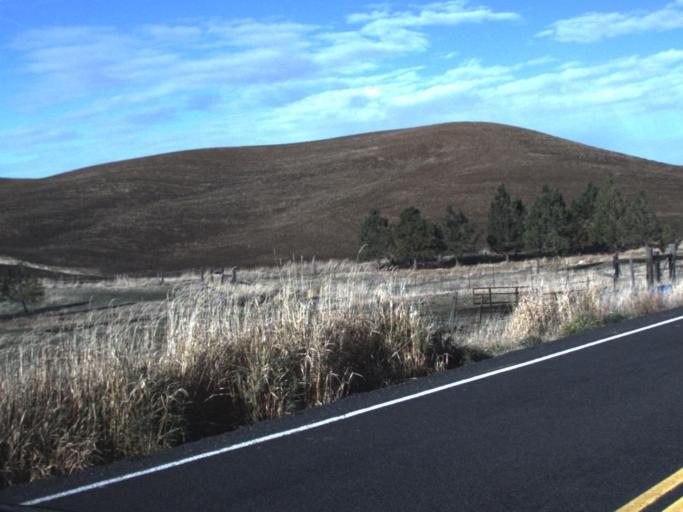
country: US
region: Washington
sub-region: Whitman County
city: Pullman
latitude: 46.7145
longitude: -117.2784
